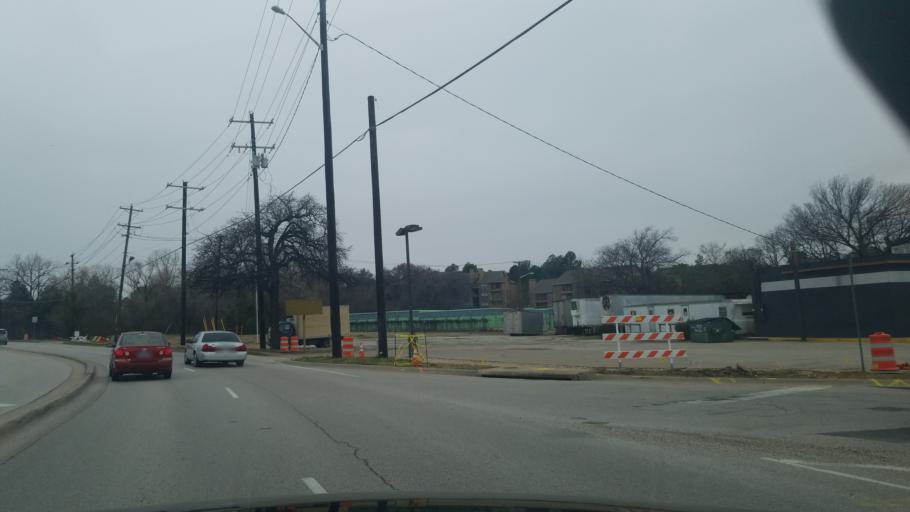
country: US
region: Texas
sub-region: Denton County
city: Denton
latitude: 33.1985
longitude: -97.1234
